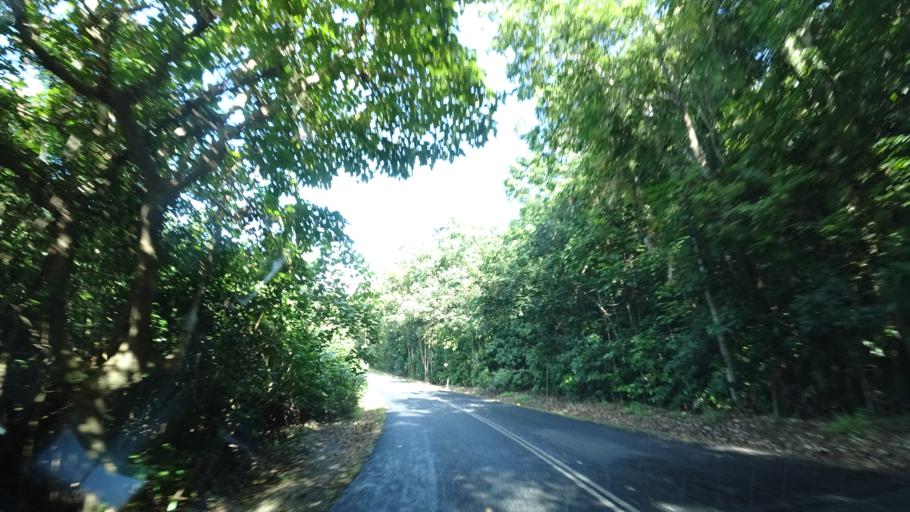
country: AU
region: Queensland
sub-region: Cairns
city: Port Douglas
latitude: -16.1309
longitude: 145.4530
